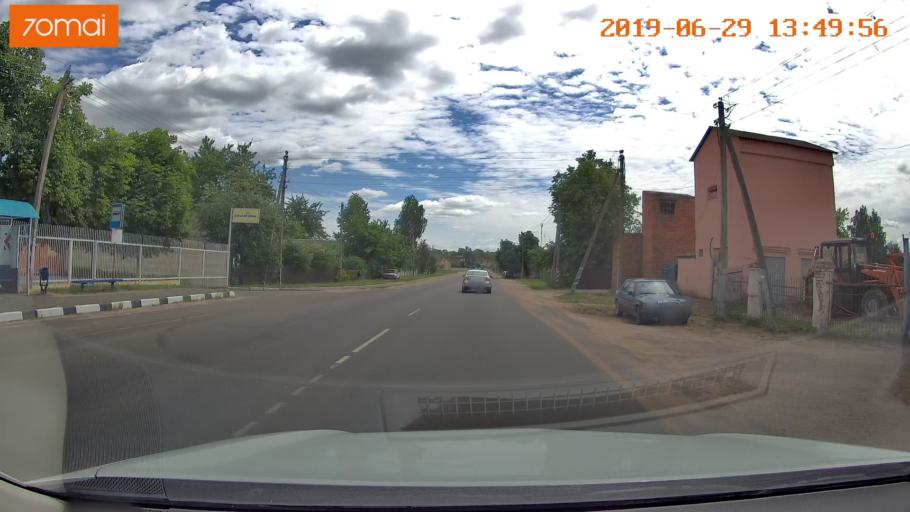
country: BY
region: Minsk
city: Slutsk
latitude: 53.0063
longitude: 27.5660
